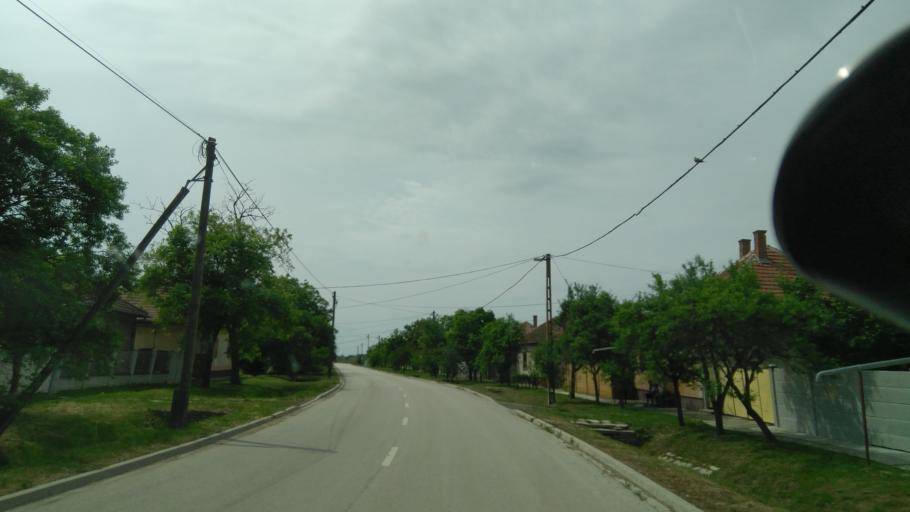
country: HU
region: Bekes
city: Mehkerek
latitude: 46.8671
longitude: 21.5154
